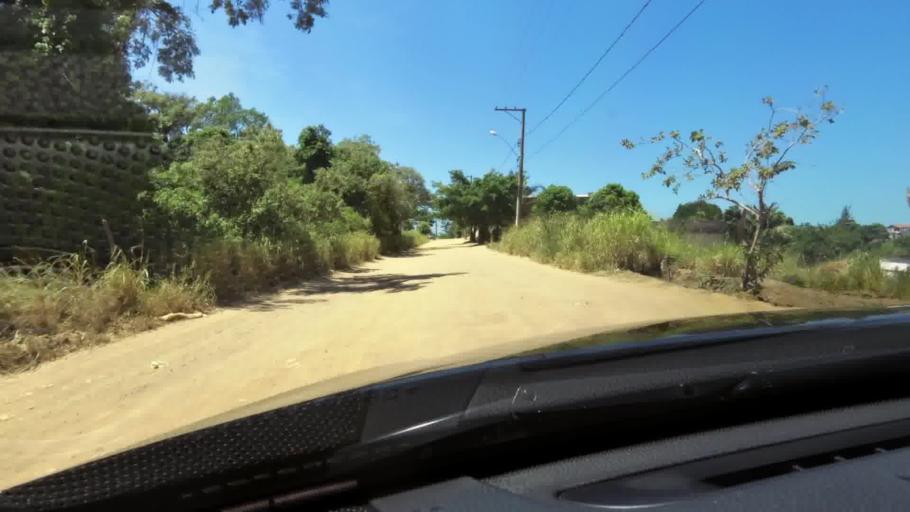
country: BR
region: Espirito Santo
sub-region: Guarapari
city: Guarapari
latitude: -20.6158
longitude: -40.4635
